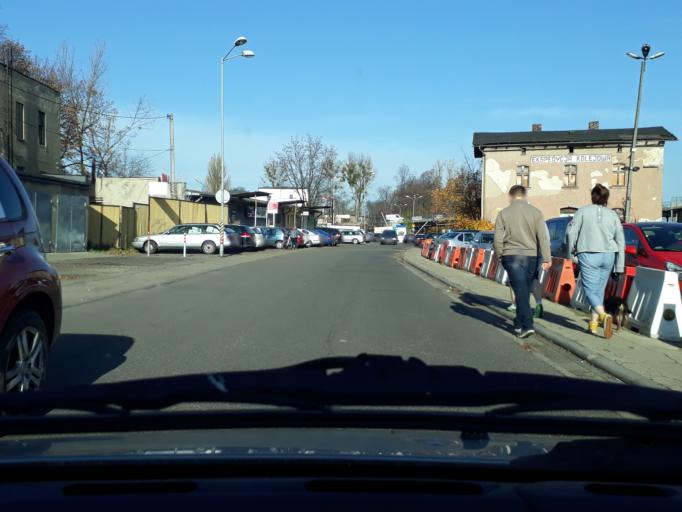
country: PL
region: Silesian Voivodeship
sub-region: Powiat tarnogorski
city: Tarnowskie Gory
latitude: 50.4434
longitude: 18.8624
